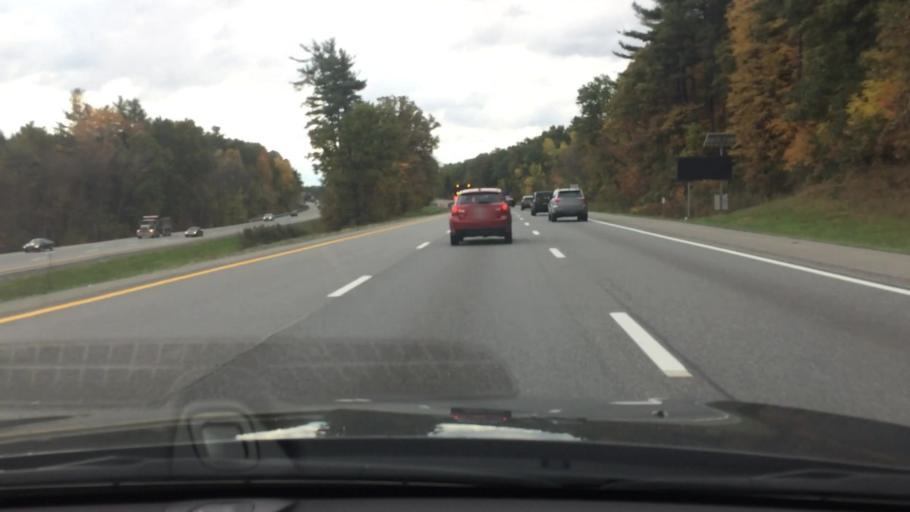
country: US
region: New York
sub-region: Albany County
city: Cohoes
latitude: 42.8299
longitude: -73.7701
